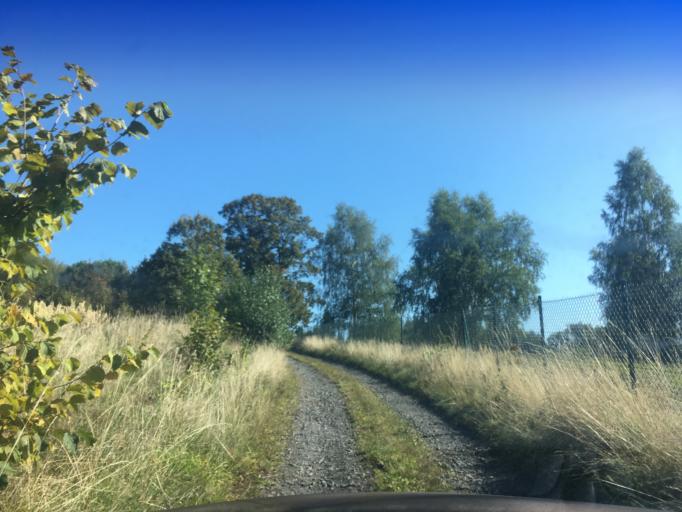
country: PL
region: Lower Silesian Voivodeship
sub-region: Powiat lubanski
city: Lesna
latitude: 50.9789
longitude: 15.2945
